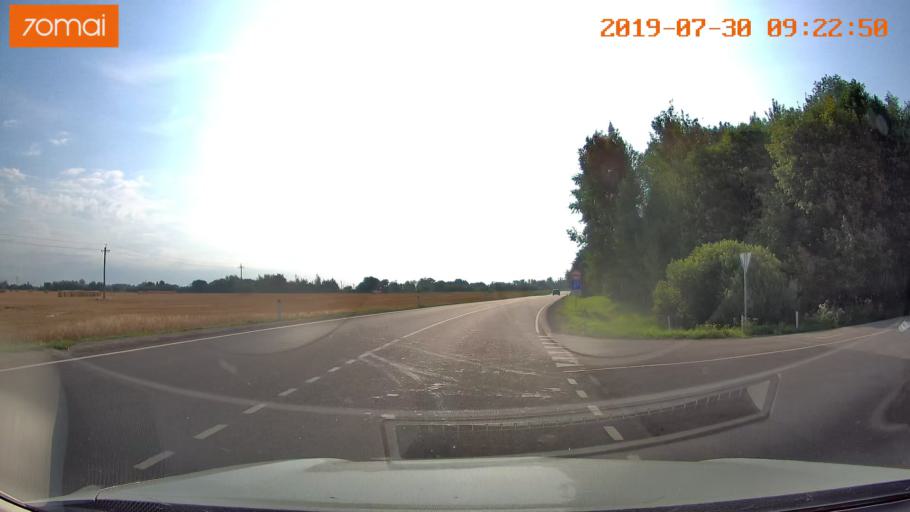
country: RU
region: Kaliningrad
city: Nesterov
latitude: 54.6338
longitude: 22.6634
